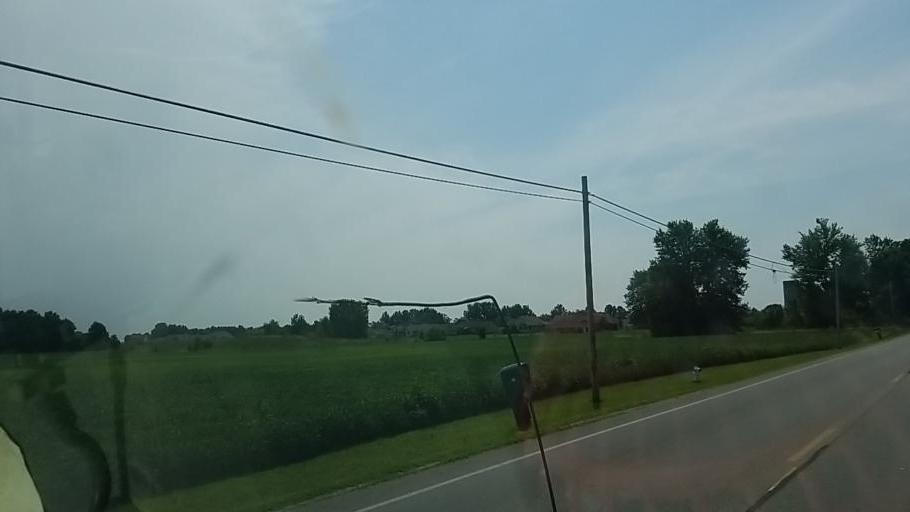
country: US
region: Ohio
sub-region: Marion County
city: Marion
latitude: 40.5915
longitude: -83.0736
